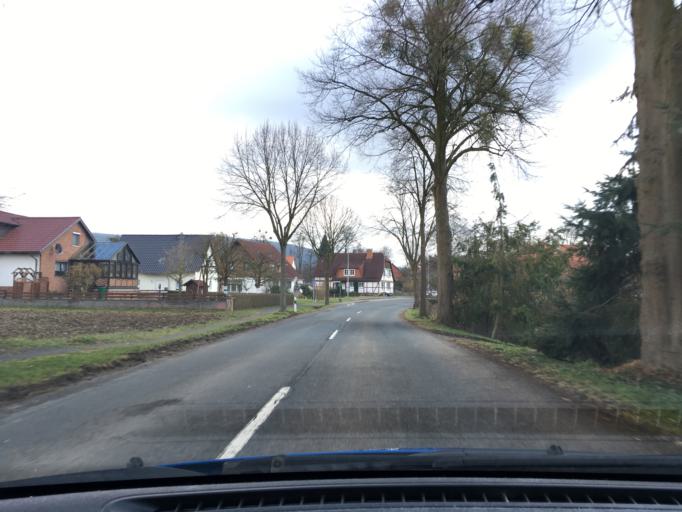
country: DE
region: Lower Saxony
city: Buhren
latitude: 51.5030
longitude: 9.6058
